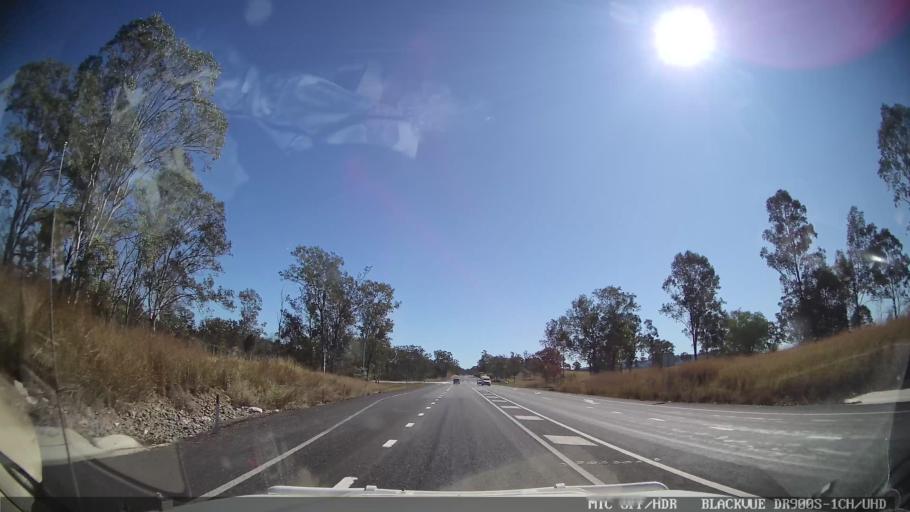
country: AU
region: Queensland
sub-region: Gympie Regional Council
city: Gympie
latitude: -26.0363
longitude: 152.5687
